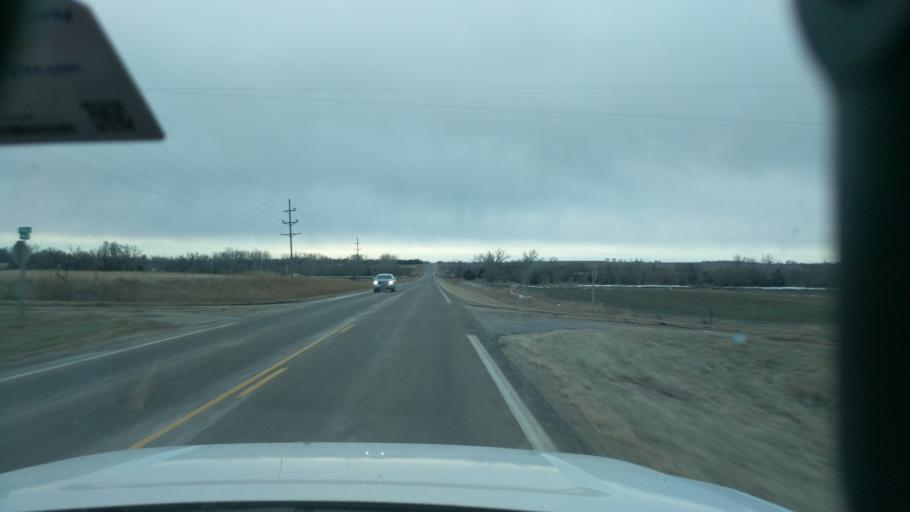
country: US
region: Kansas
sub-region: Marion County
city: Hillsboro
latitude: 38.3483
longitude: -97.3350
